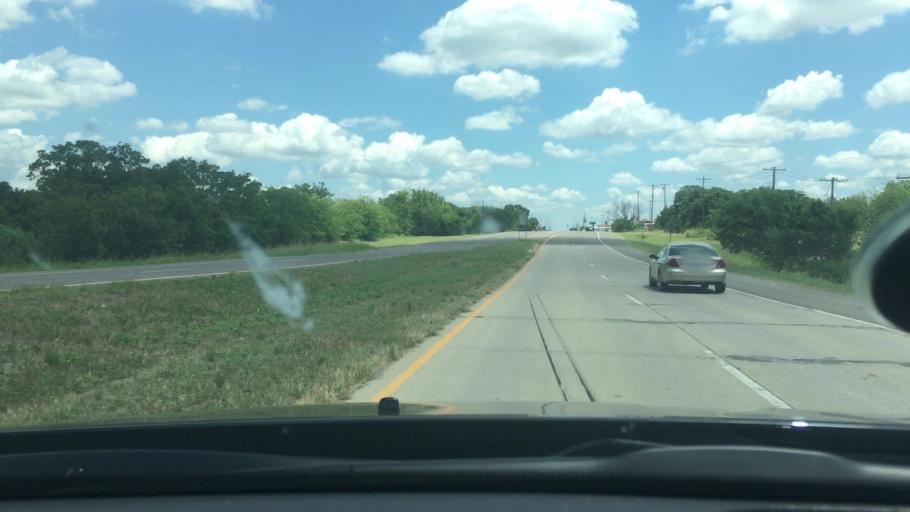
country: US
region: Oklahoma
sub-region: Carter County
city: Lone Grove
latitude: 34.1730
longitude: -97.2718
